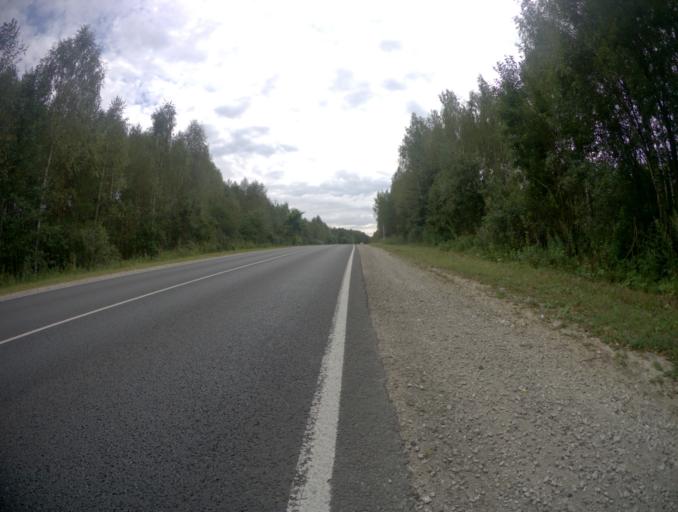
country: RU
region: Vladimir
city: Golovino
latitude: 55.9490
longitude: 40.5779
